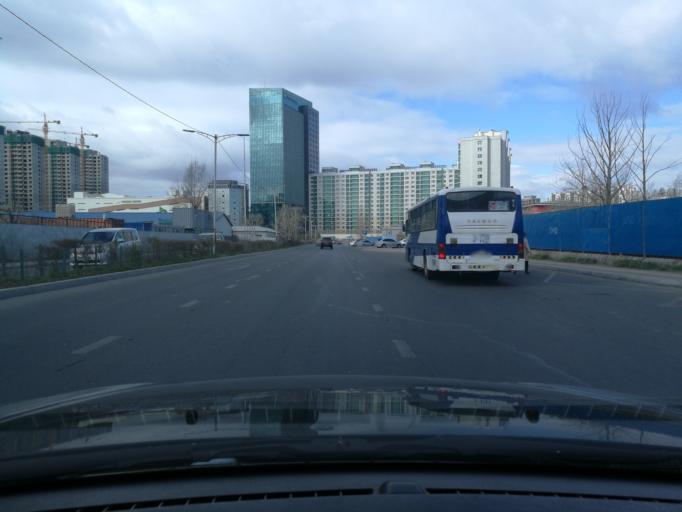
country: MN
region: Ulaanbaatar
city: Ulaanbaatar
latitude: 47.9043
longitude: 106.9175
